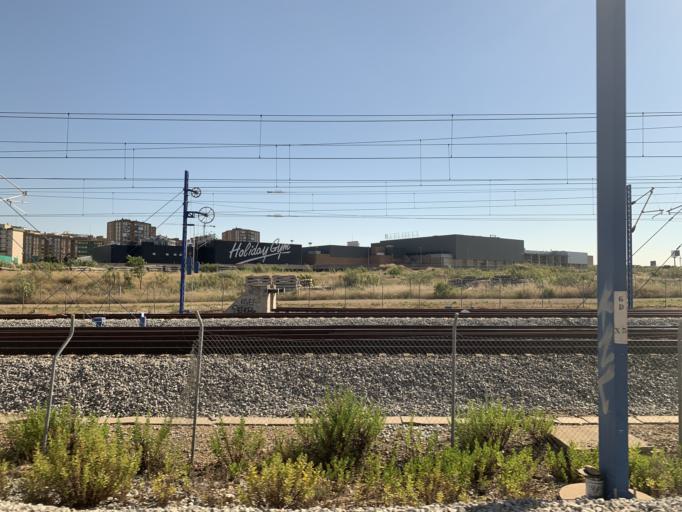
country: ES
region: Aragon
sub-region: Provincia de Zaragoza
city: Delicias
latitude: 41.6617
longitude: -0.9182
